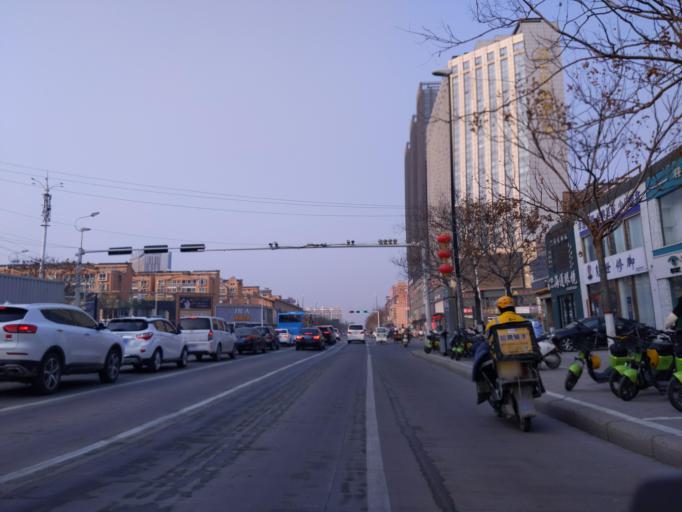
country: CN
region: Henan Sheng
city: Zhongyuanlu
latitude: 35.7697
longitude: 115.0586
